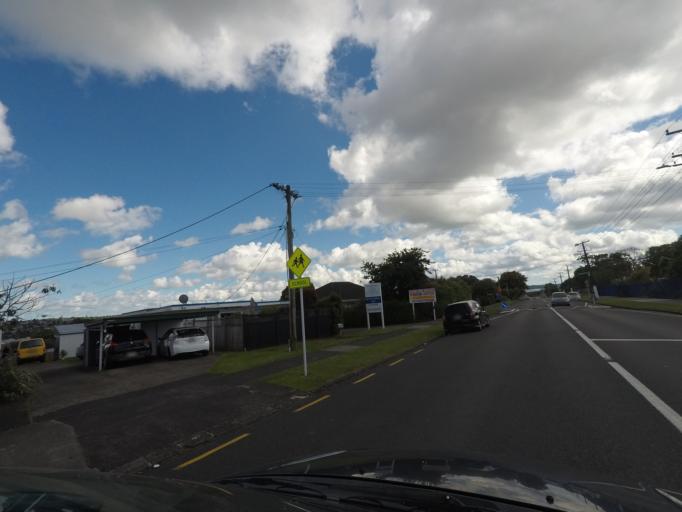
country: NZ
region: Auckland
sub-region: Auckland
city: Waitakere
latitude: -36.9064
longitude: 174.6634
